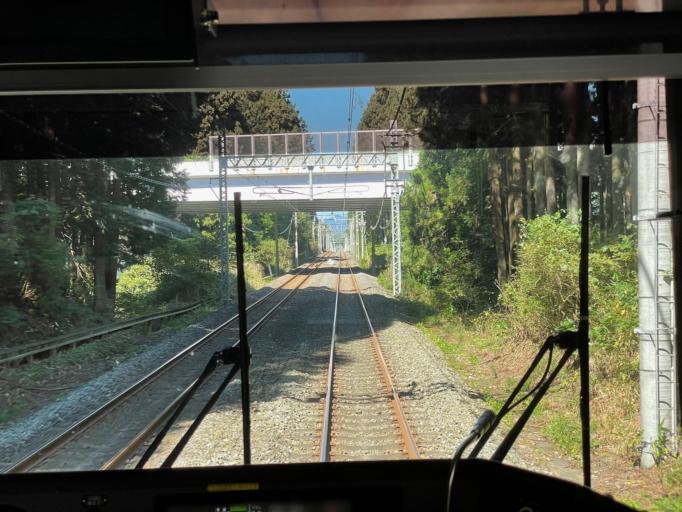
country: JP
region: Tochigi
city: Imaichi
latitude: 36.6999
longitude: 139.7096
